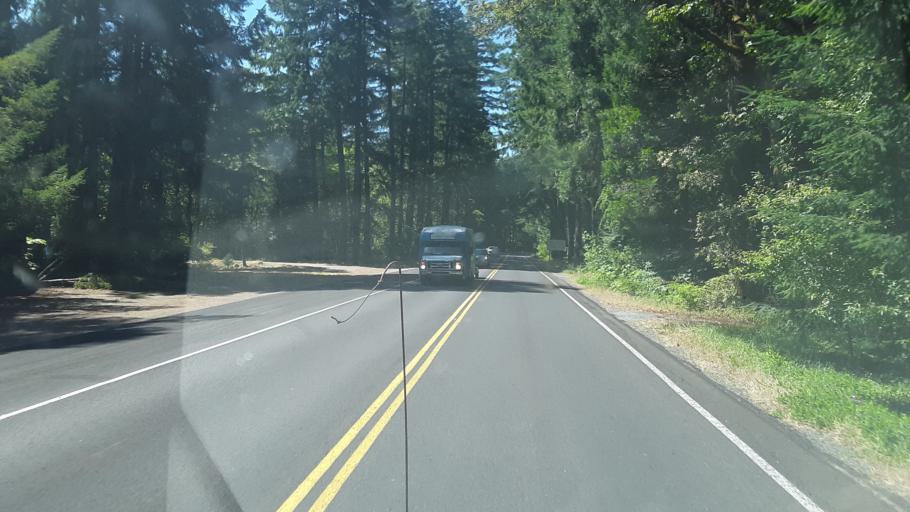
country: US
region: Oregon
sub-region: Josephine County
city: Cave Junction
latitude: 41.9873
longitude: -123.7179
